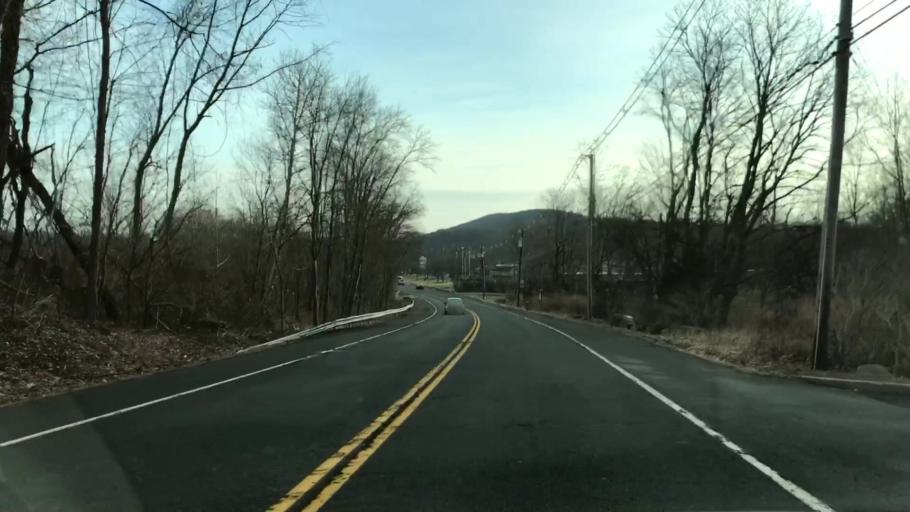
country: US
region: New York
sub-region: Rockland County
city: Pomona
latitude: 41.1822
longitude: -74.0517
